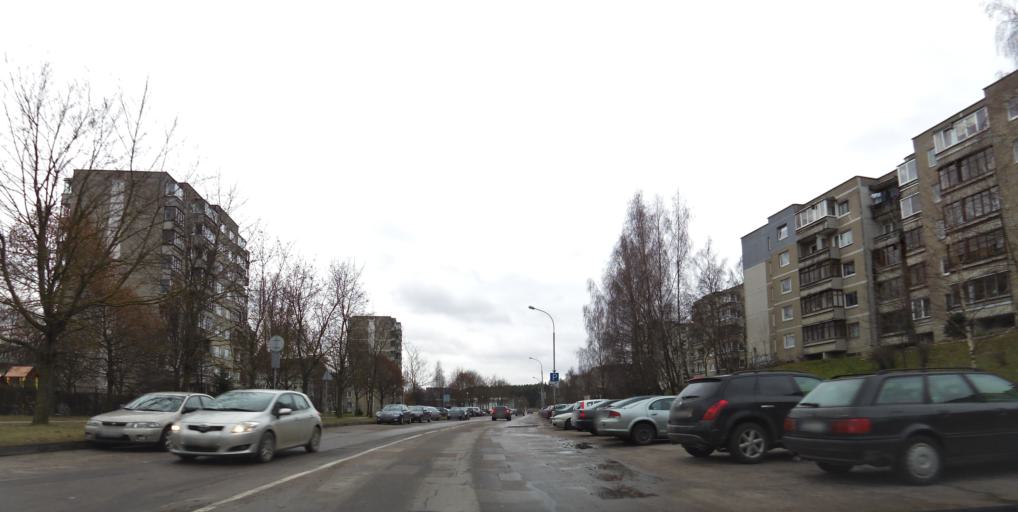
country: LT
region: Vilnius County
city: Justiniskes
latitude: 54.7191
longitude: 25.2294
